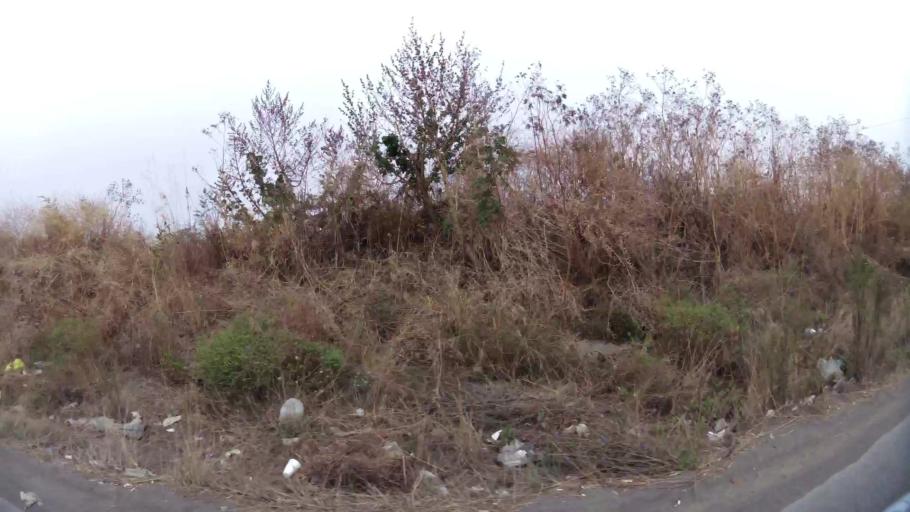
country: CL
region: Biobio
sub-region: Provincia de Concepcion
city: Concepcion
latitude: -36.7969
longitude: -73.0828
